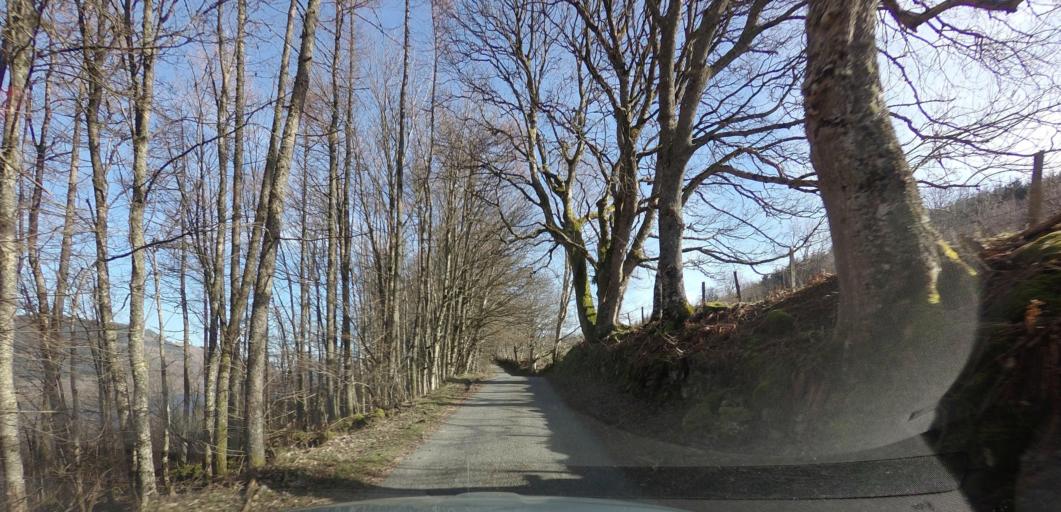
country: GB
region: Scotland
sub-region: Perth and Kinross
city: Comrie
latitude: 56.5600
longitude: -4.0687
